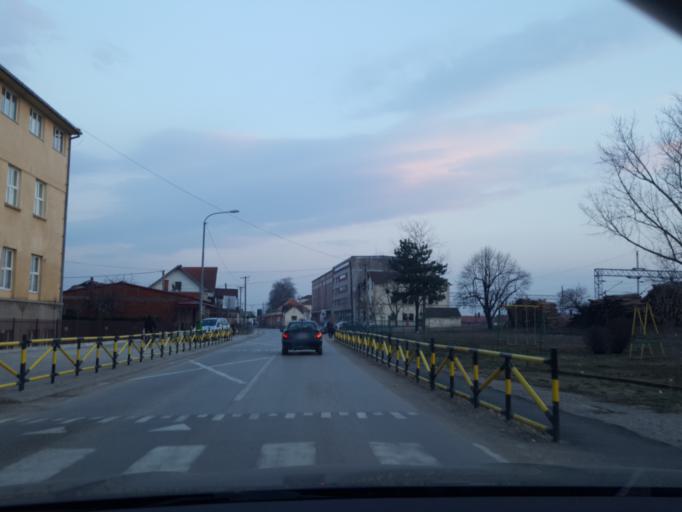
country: RS
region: Central Serbia
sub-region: Nisavski Okrug
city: Aleksinac
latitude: 43.5075
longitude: 21.6952
